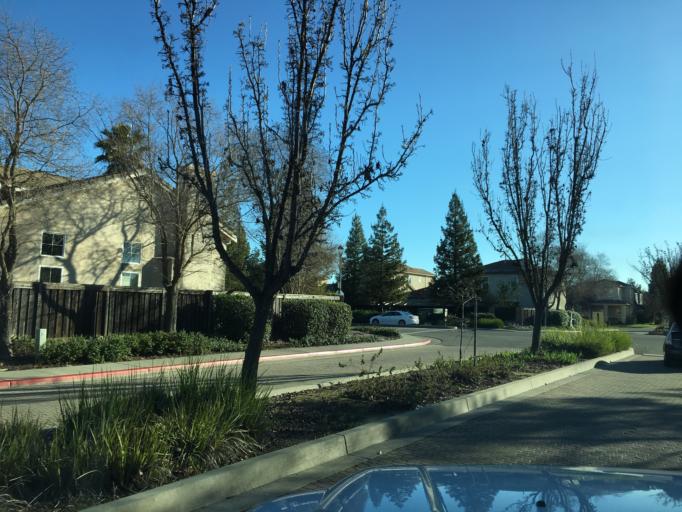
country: US
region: California
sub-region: Yolo County
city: Davis
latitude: 38.5571
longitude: -121.7719
